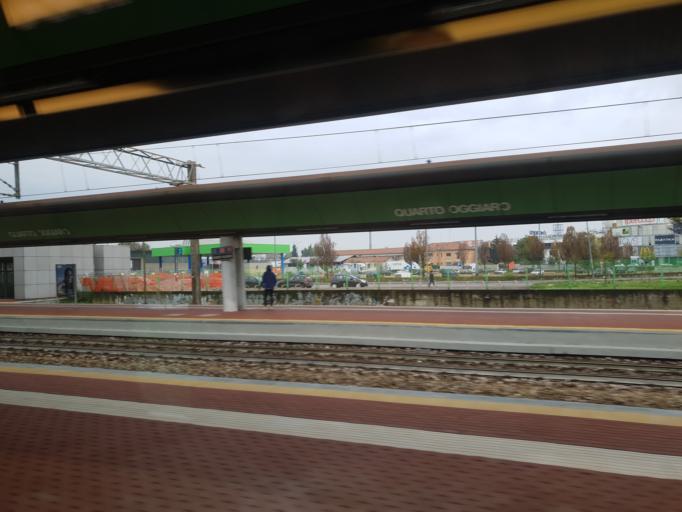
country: IT
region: Lombardy
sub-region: Citta metropolitana di Milano
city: Novate Milanese
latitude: 45.5187
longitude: 9.1456
